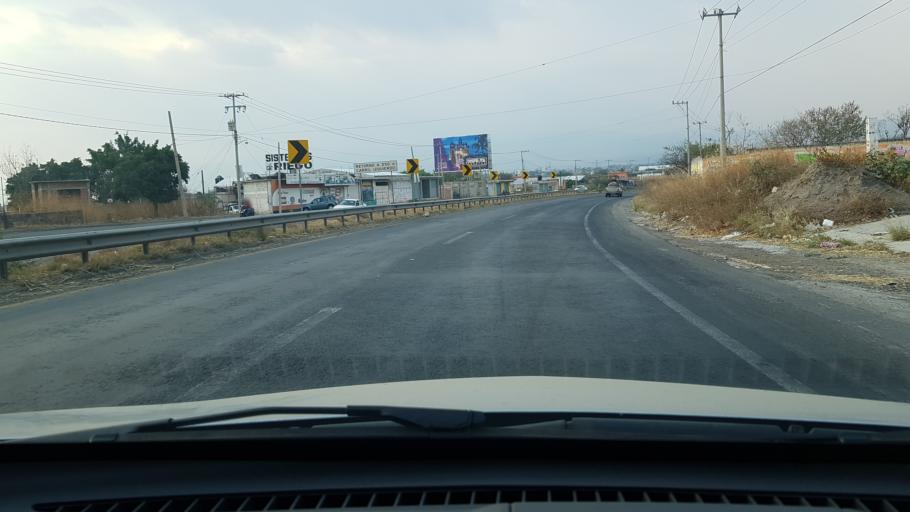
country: MX
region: Morelos
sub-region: Yecapixtla
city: Juan Morales
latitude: 18.8231
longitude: -98.9216
